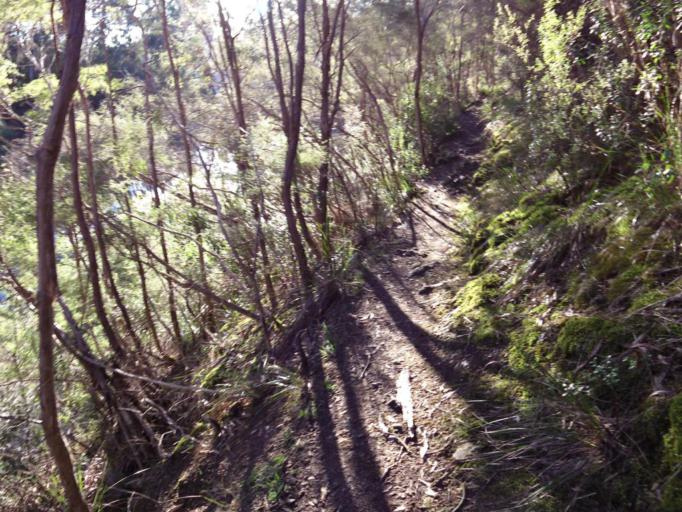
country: AU
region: Victoria
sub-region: Manningham
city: Warrandyte
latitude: -37.7334
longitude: 145.2430
